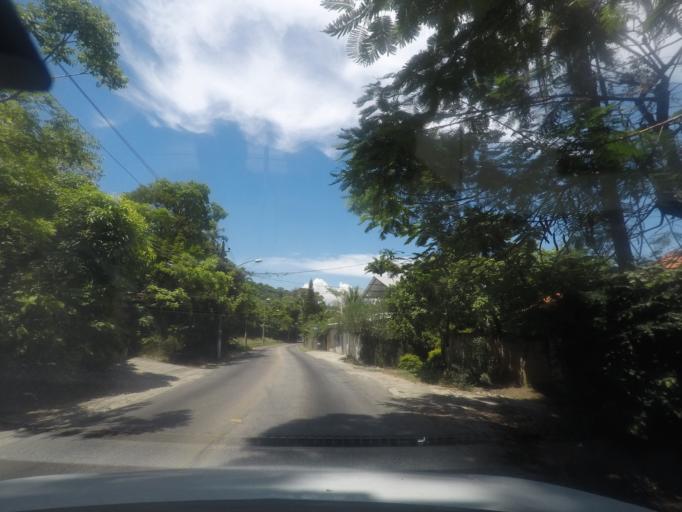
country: BR
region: Rio de Janeiro
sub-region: Itaguai
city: Itaguai
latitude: -23.0007
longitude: -43.6451
